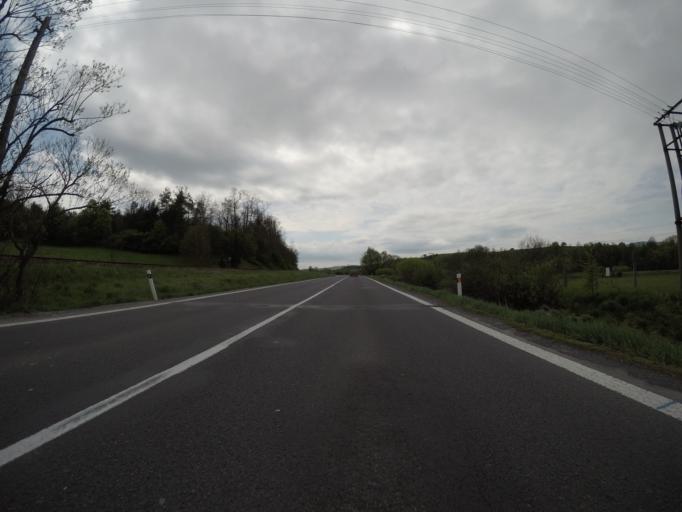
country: SK
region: Banskobystricky
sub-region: Okres Banska Bystrica
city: Zvolen
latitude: 48.5047
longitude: 19.0976
